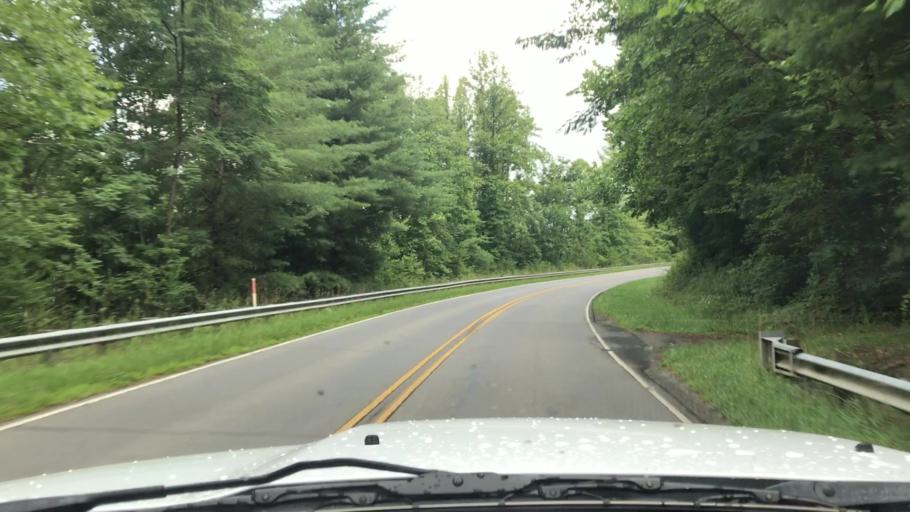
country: US
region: North Carolina
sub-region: Graham County
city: Robbinsville
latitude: 35.3438
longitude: -83.8143
